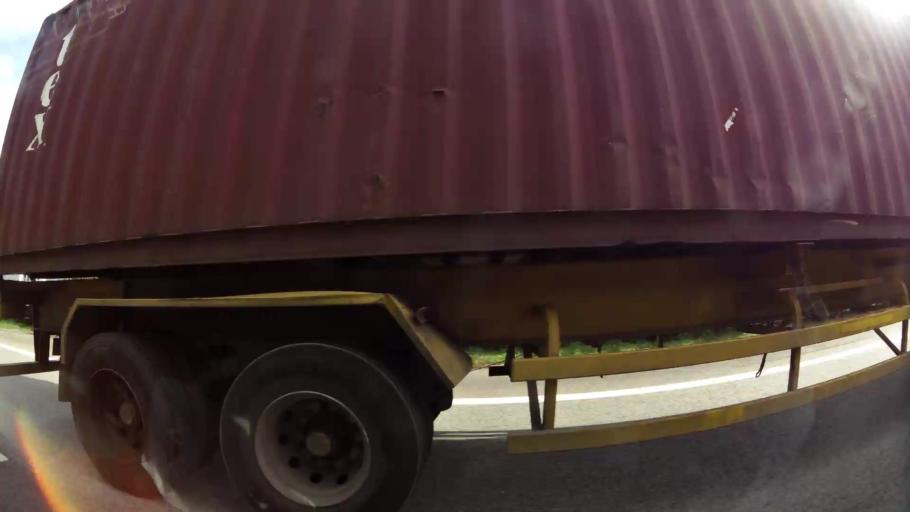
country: MY
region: Johor
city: Johor Bahru
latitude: 1.3348
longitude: 103.6512
